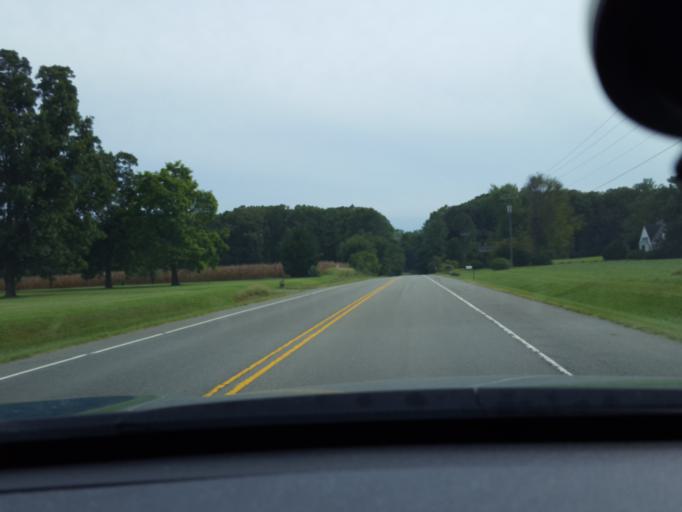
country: US
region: Virginia
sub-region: Hanover County
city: Hanover
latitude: 37.7057
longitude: -77.3840
